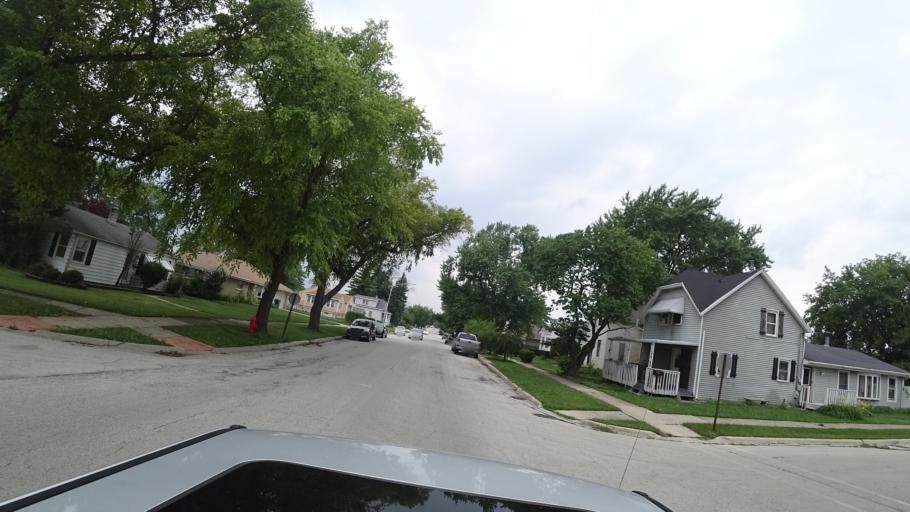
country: US
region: Illinois
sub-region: Cook County
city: Chicago Ridge
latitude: 41.7011
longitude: -87.7755
